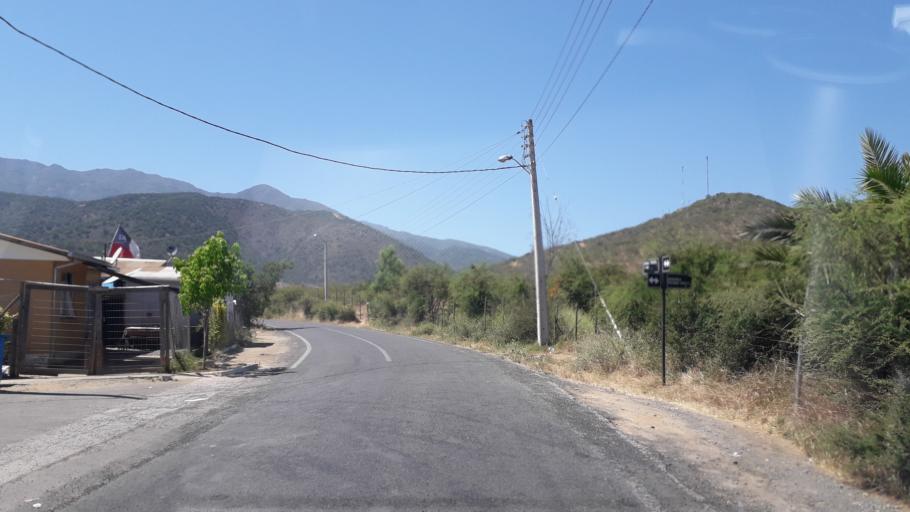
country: CL
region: Valparaiso
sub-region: Provincia de Marga Marga
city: Limache
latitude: -33.0667
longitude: -71.2220
